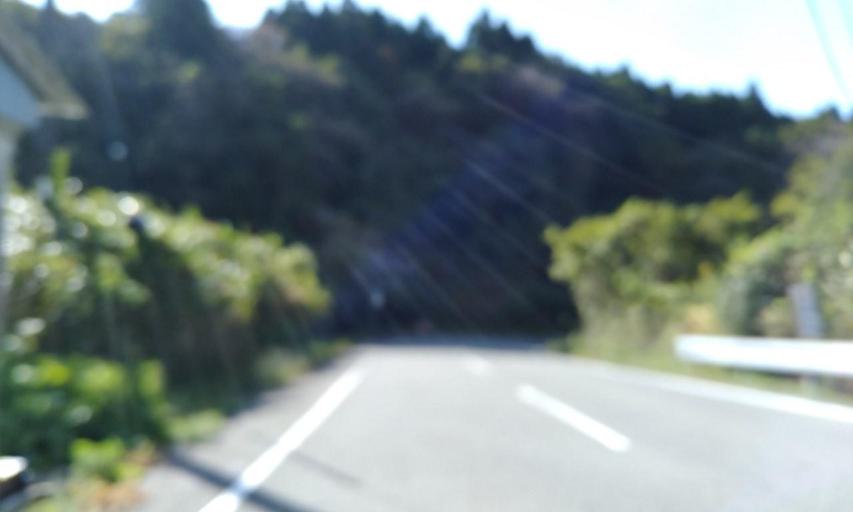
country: JP
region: Wakayama
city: Iwade
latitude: 34.1151
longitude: 135.3461
